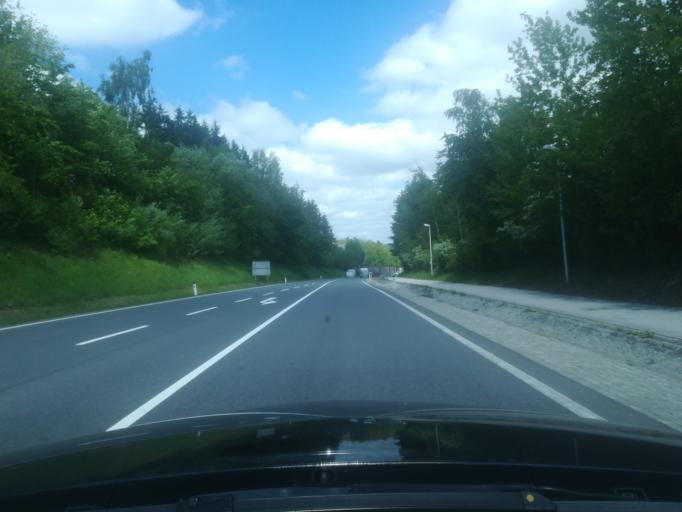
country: AT
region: Upper Austria
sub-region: Politischer Bezirk Urfahr-Umgebung
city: Engerwitzdorf
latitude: 48.3498
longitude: 14.5253
